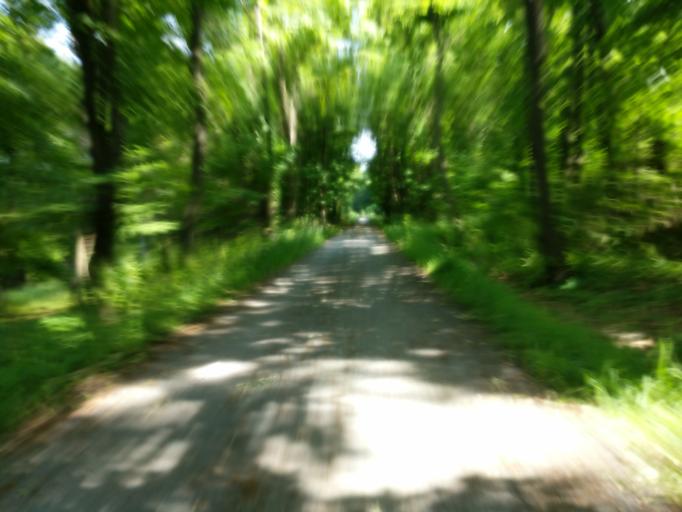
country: US
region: New York
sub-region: Tompkins County
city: Northwest Ithaca
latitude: 42.4964
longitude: -76.5438
